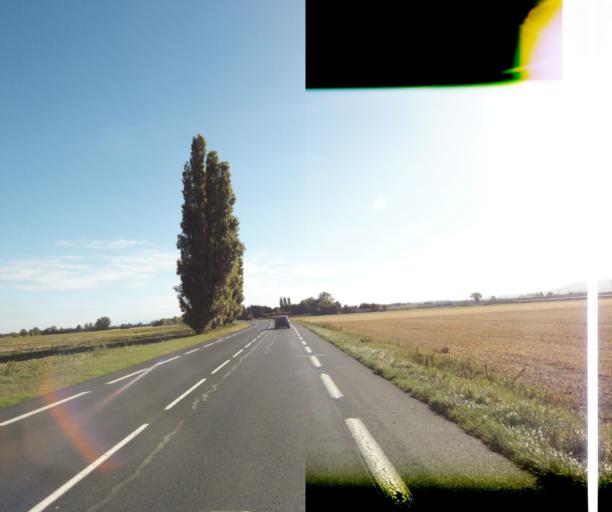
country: FR
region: Auvergne
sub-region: Departement du Puy-de-Dome
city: Aulnat
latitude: 45.8139
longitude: 3.1651
